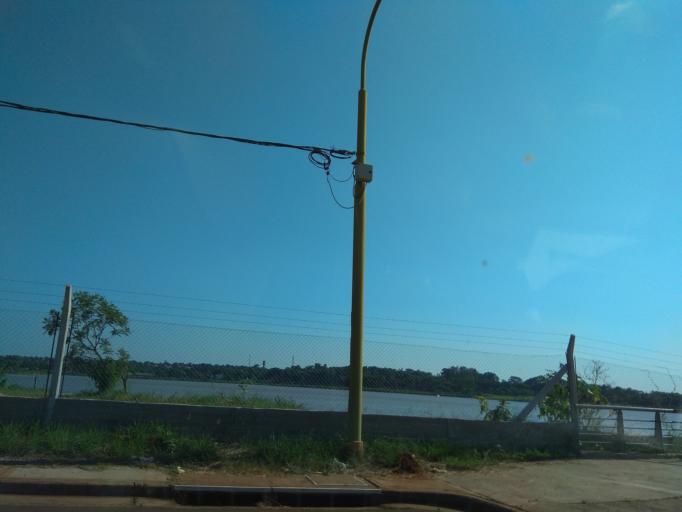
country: AR
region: Misiones
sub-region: Departamento de Capital
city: Posadas
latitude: -27.3560
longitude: -55.9423
